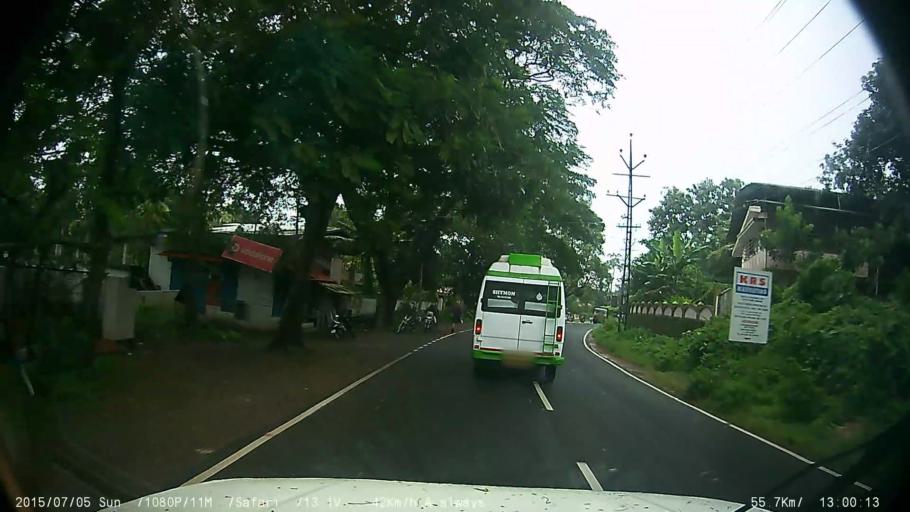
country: IN
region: Kerala
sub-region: Kottayam
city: Changanacheri
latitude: 9.4779
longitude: 76.5750
